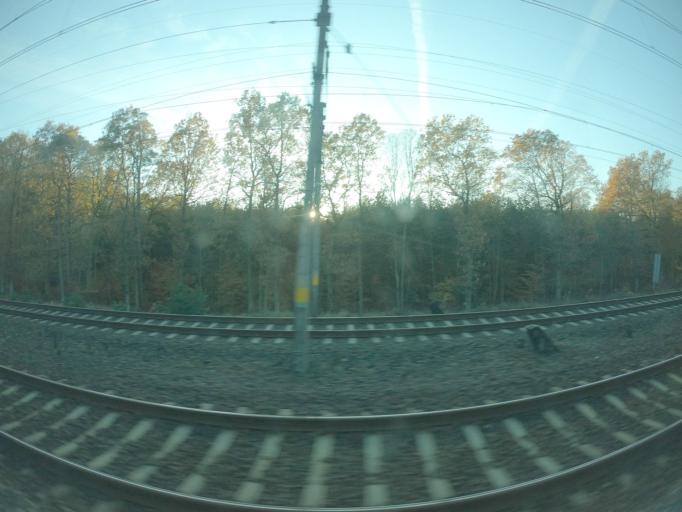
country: PL
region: Lubusz
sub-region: Powiat slubicki
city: Rzepin
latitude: 52.3216
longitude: 14.8495
